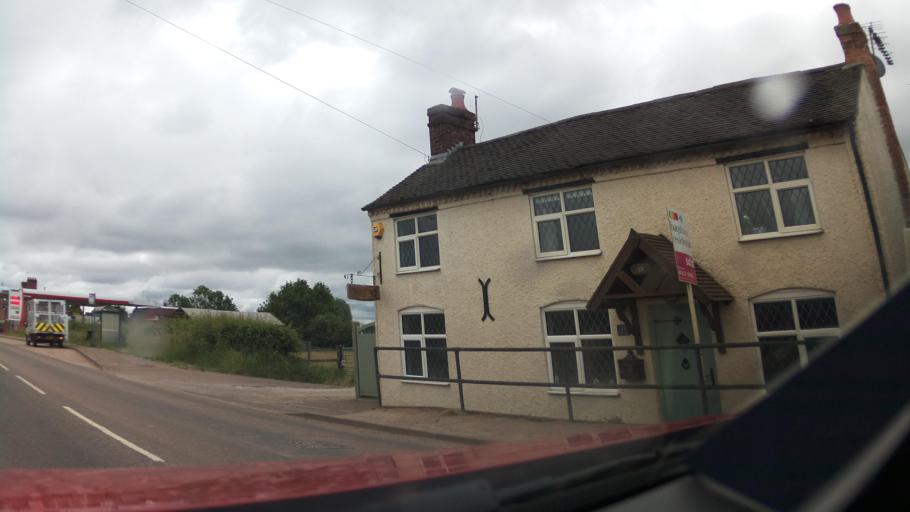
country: GB
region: England
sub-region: Staffordshire
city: Burton upon Trent
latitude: 52.8749
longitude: -1.6822
